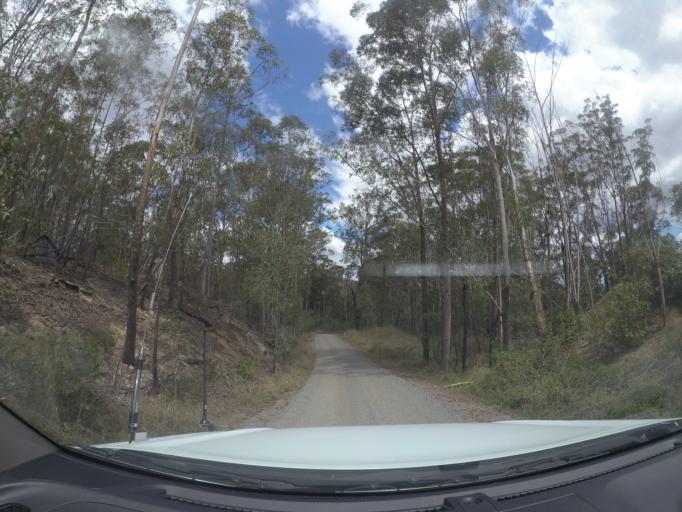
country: AU
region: Queensland
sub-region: Logan
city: Cedar Vale
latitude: -27.9030
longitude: 153.0317
